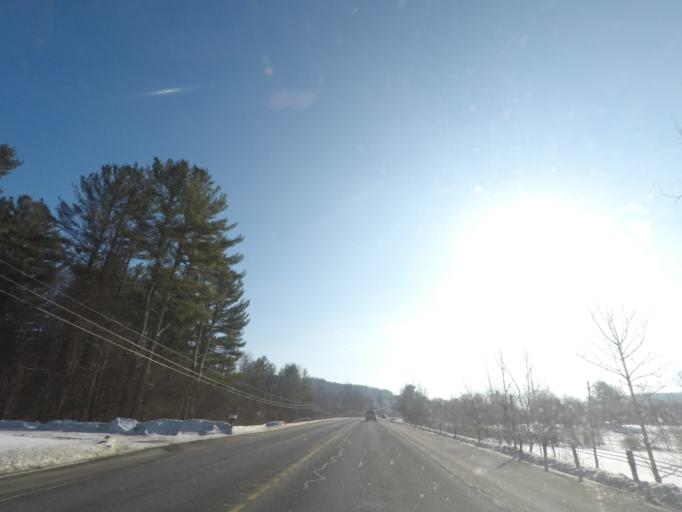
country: US
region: Massachusetts
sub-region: Berkshire County
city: Lanesborough
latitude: 42.5206
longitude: -73.3585
